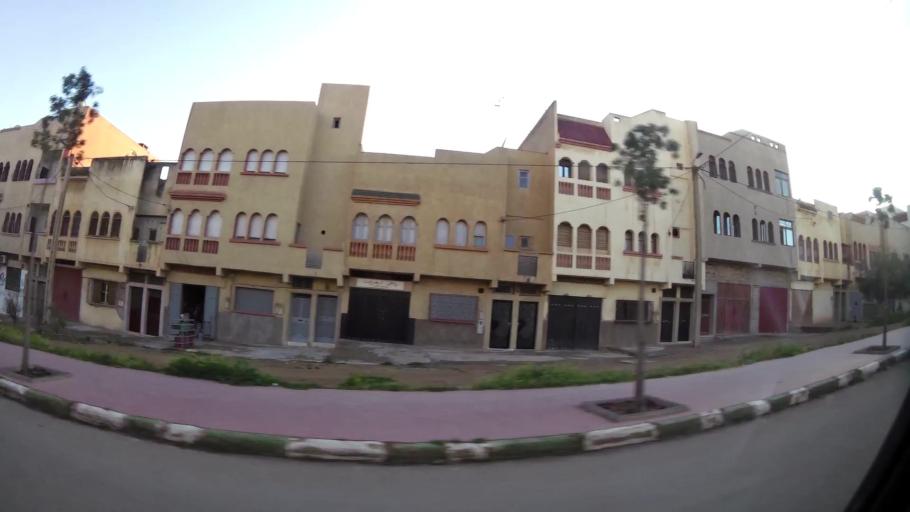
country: MA
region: Chaouia-Ouardigha
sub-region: Settat Province
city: Settat
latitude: 32.9892
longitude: -7.6106
